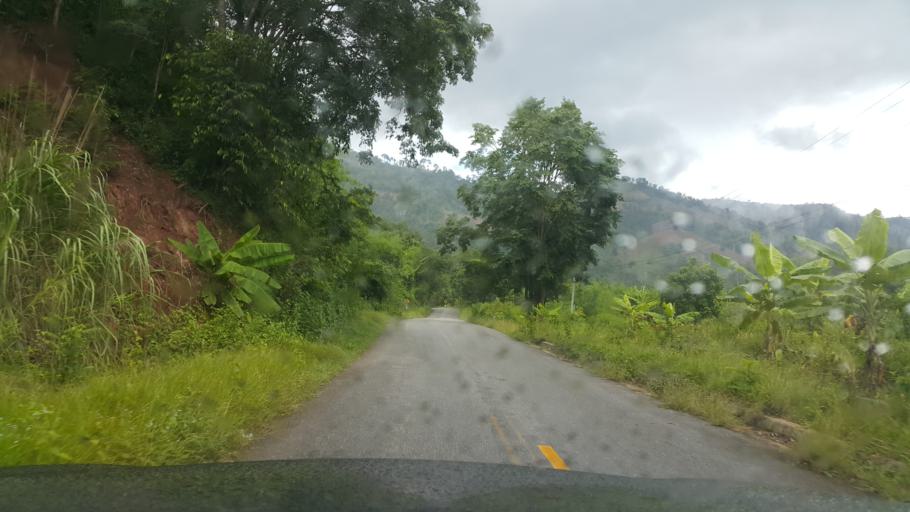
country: TH
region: Uttaradit
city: Nam Pat
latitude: 17.5143
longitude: 100.8177
